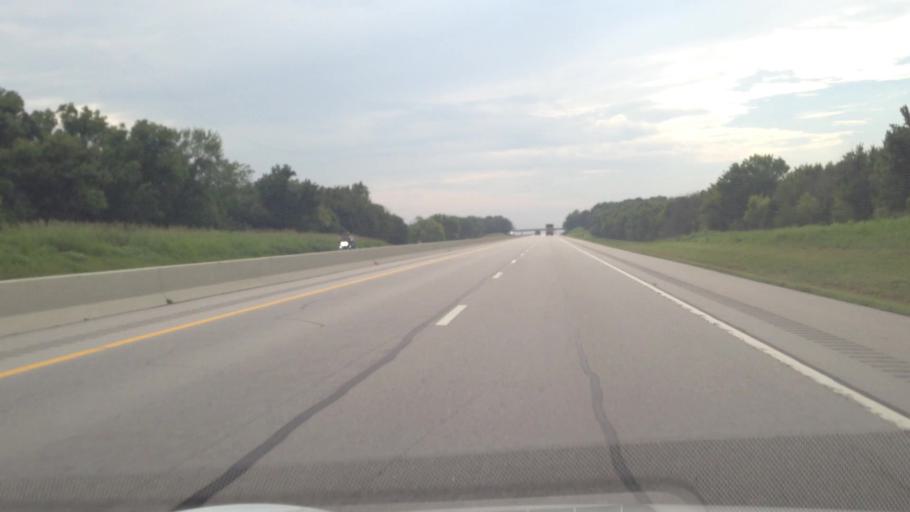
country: US
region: Kansas
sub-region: Cherokee County
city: Baxter Springs
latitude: 36.9366
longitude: -94.7041
